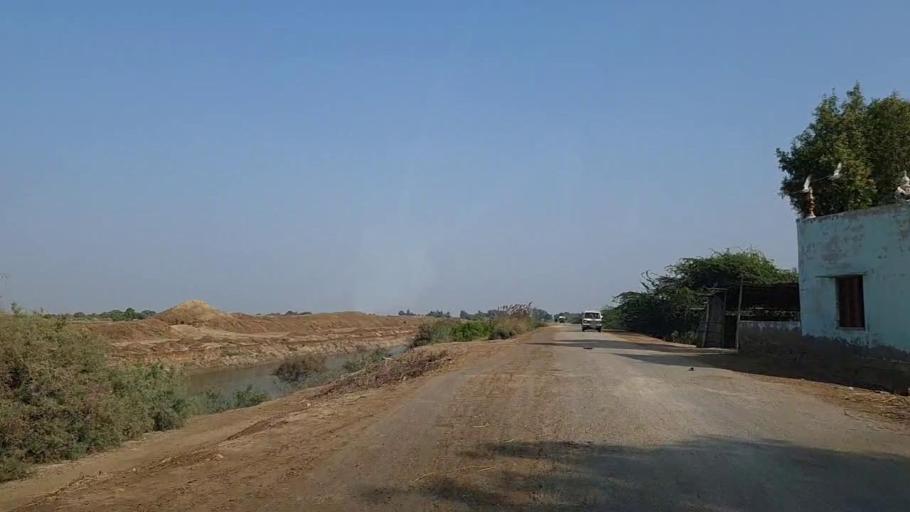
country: PK
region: Sindh
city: Mirpur Sakro
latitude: 24.6292
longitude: 67.6427
